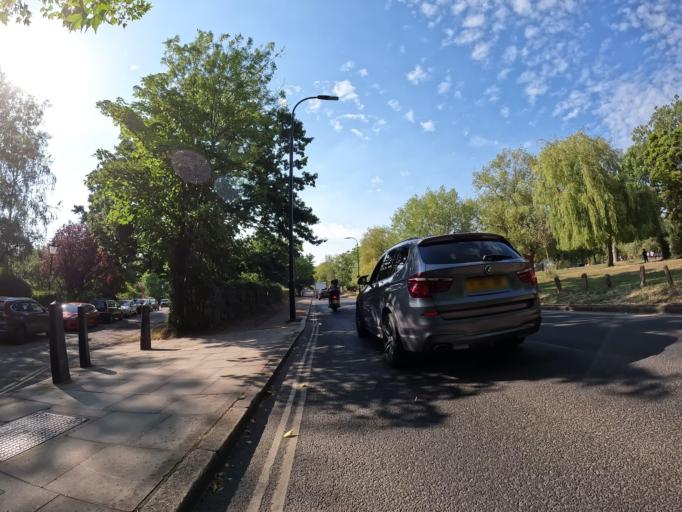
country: GB
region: England
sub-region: Greater London
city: Hadley Wood
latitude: 51.6646
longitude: -0.1686
